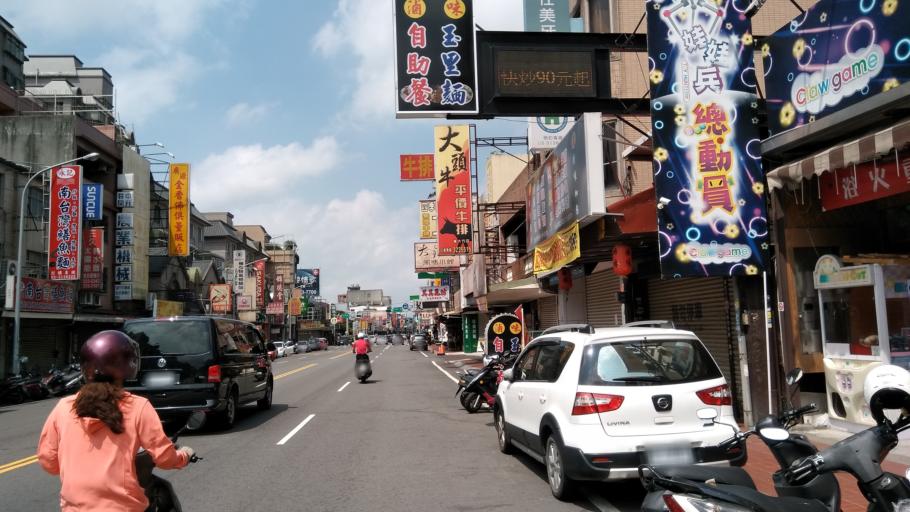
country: TW
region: Taiwan
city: Taoyuan City
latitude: 25.0220
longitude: 121.2625
